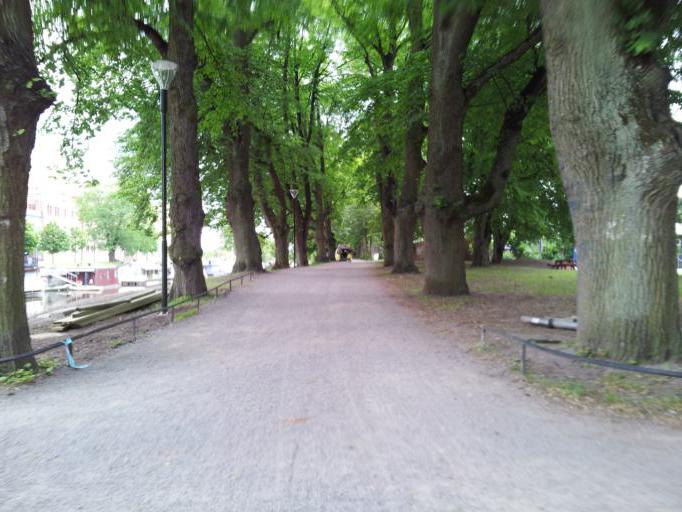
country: SE
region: Uppsala
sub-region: Uppsala Kommun
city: Uppsala
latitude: 59.8519
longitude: 17.6450
